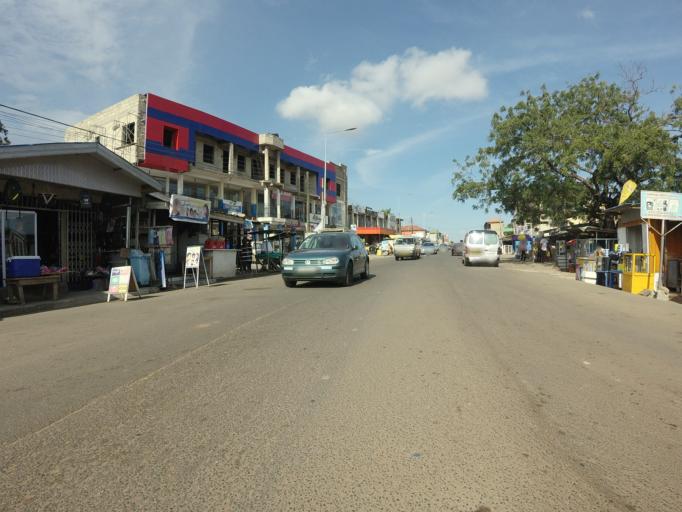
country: GH
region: Greater Accra
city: Medina Estates
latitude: 5.6421
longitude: -0.1651
